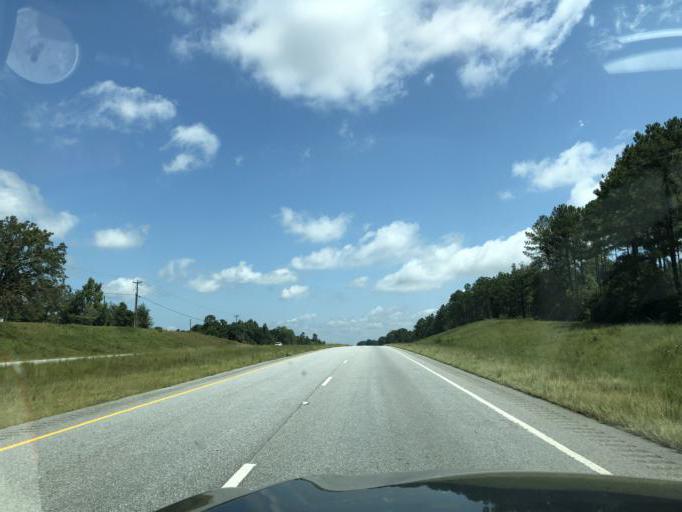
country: US
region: Alabama
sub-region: Barbour County
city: Eufaula
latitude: 31.7543
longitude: -85.2179
